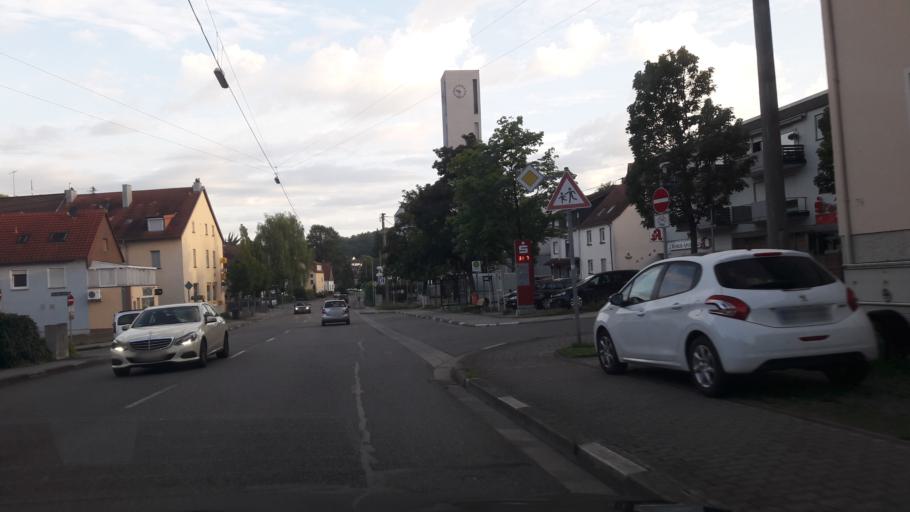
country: DE
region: Saarland
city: Kleinblittersdorf
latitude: 49.1980
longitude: 7.0661
